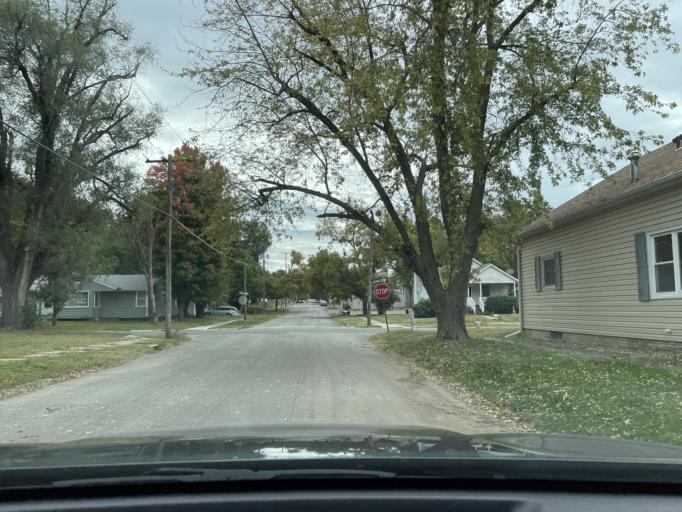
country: US
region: Missouri
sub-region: Buchanan County
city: Saint Joseph
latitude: 39.7695
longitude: -94.8224
